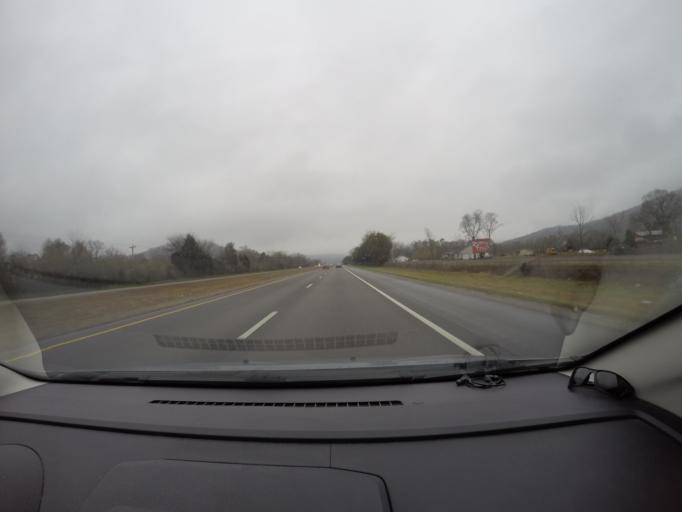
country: US
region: Tennessee
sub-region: Marion County
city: Kimball
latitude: 35.0846
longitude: -85.7368
